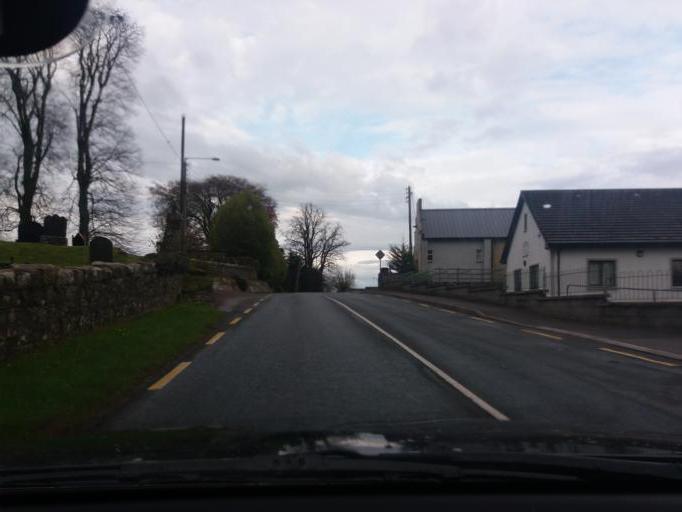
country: IE
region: Ulster
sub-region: An Cabhan
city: Ballyconnell
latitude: 54.1176
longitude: -7.5877
